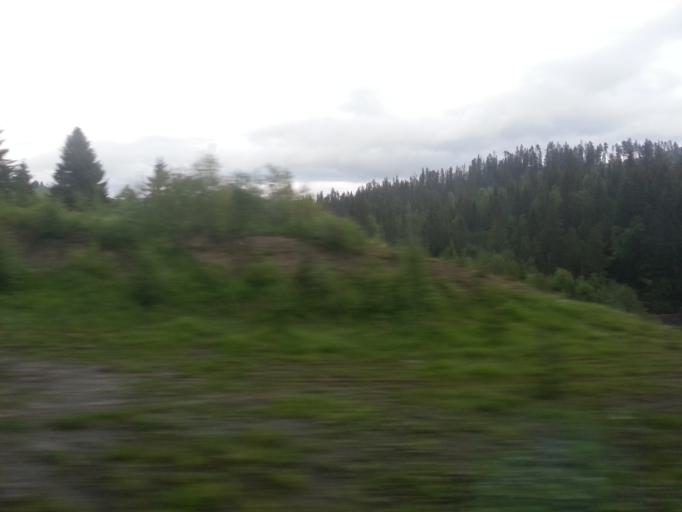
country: NO
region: Sor-Trondelag
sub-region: Midtre Gauldal
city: Storen
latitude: 62.9261
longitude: 10.1542
